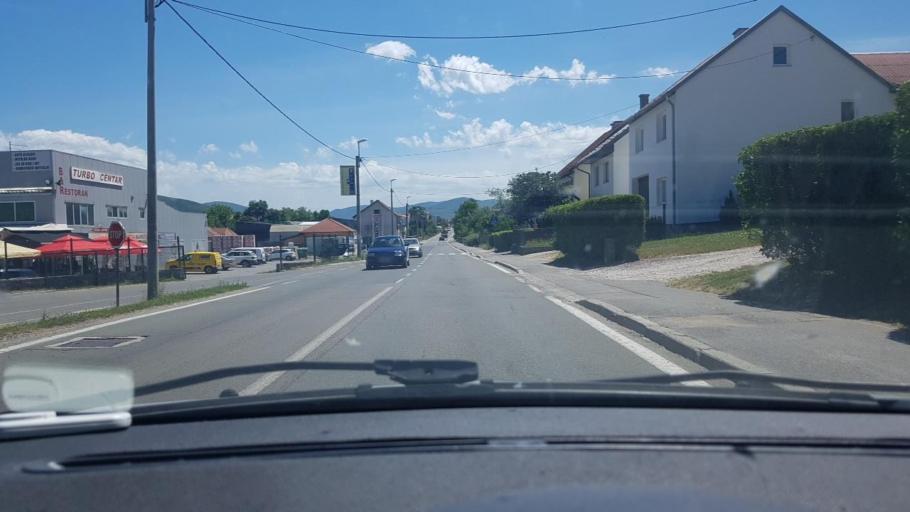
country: HR
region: Licko-Senjska
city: Otocac
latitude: 44.8677
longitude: 15.2499
